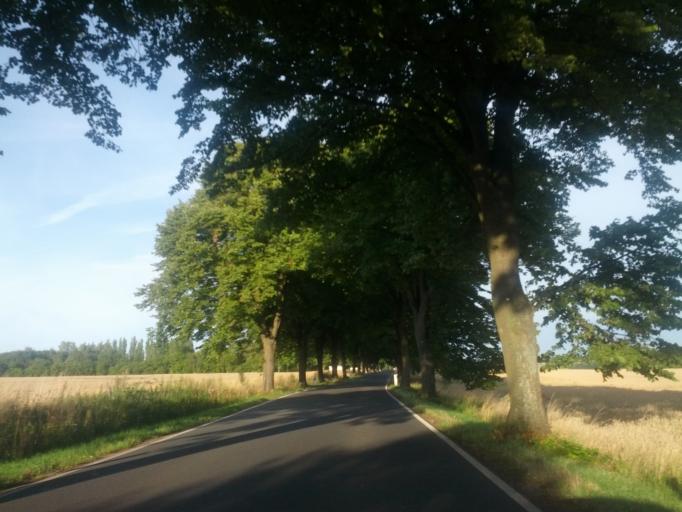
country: DE
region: Mecklenburg-Vorpommern
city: Bastorf
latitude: 54.1069
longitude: 11.6318
